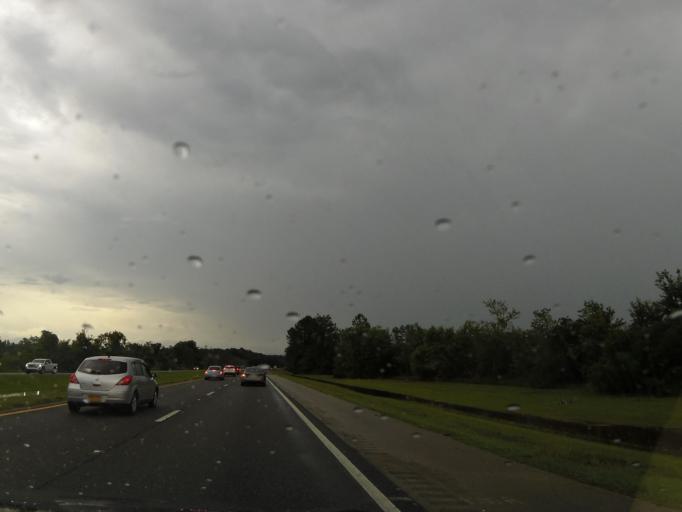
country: US
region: Florida
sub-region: Duval County
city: Baldwin
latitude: 30.2994
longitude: -81.9309
